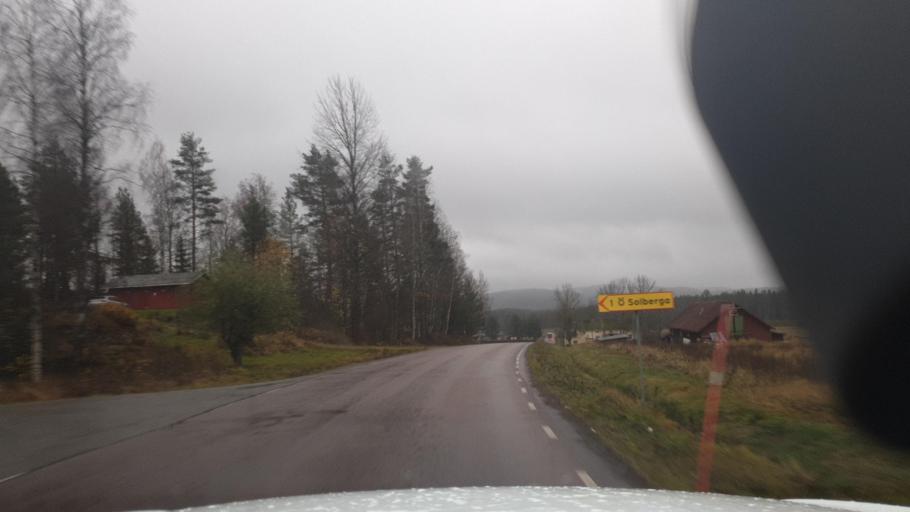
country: SE
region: Vaermland
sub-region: Eda Kommun
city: Charlottenberg
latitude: 59.7437
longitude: 12.1666
